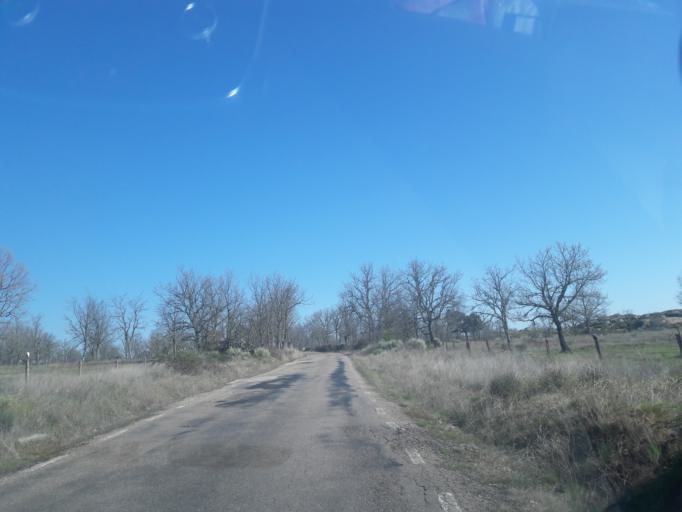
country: ES
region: Castille and Leon
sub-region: Provincia de Salamanca
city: Valsalabroso
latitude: 41.1129
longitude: -6.4835
